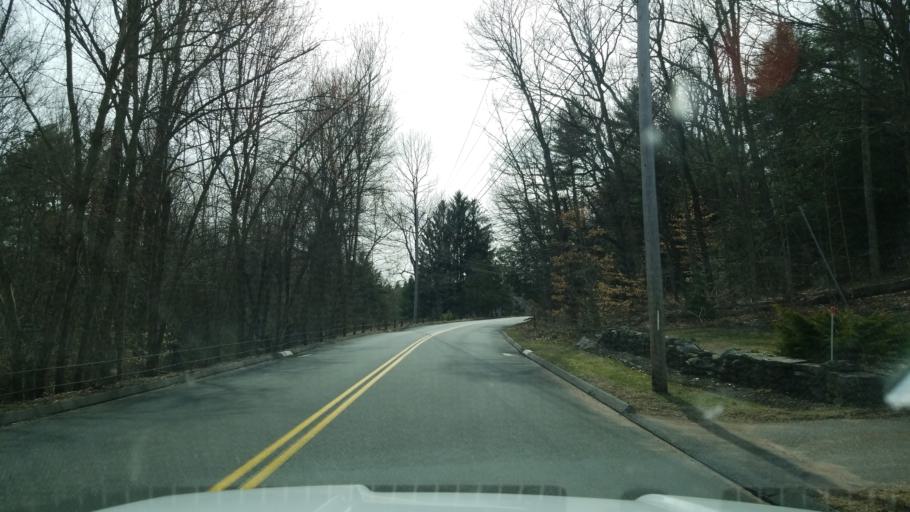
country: US
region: Connecticut
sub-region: Hartford County
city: Glastonbury Center
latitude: 41.6673
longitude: -72.5777
